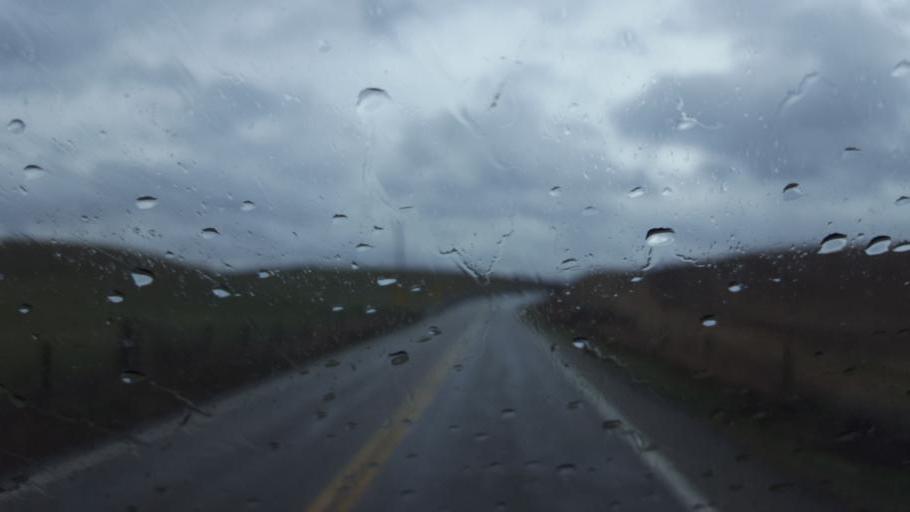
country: US
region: Ohio
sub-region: Ashland County
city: Loudonville
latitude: 40.6117
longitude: -82.1621
